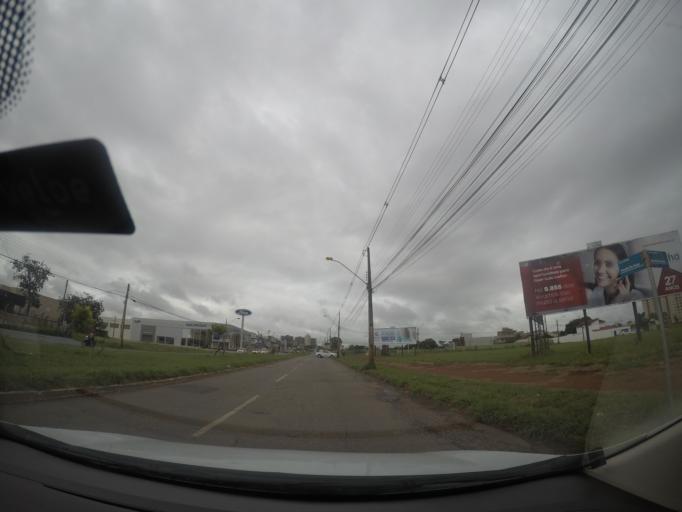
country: BR
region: Goias
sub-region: Goiania
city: Goiania
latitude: -16.7471
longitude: -49.2931
